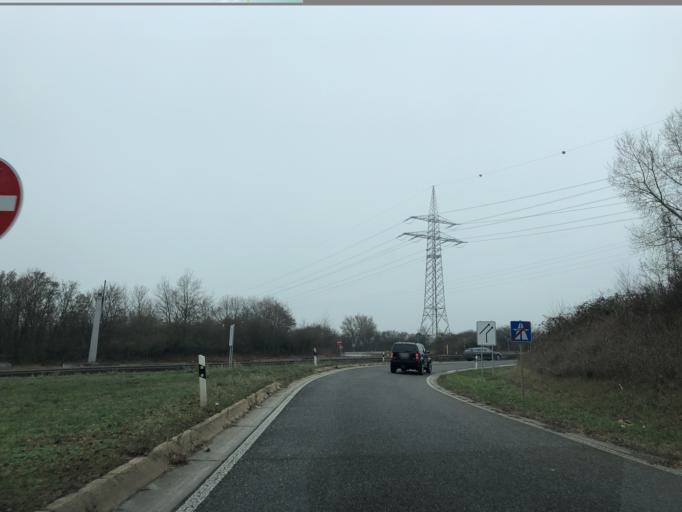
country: DE
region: Rheinland-Pfalz
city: Mainz
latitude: 50.0319
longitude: 8.2958
